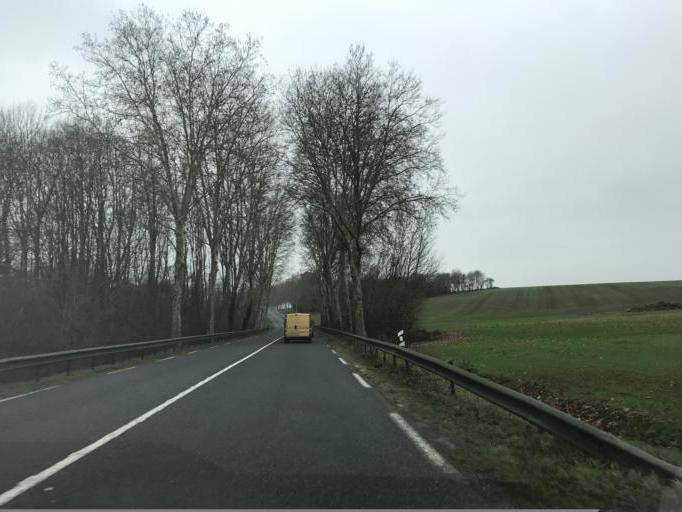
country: FR
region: Bourgogne
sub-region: Departement de l'Yonne
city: Avallon
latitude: 47.5026
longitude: 3.8816
